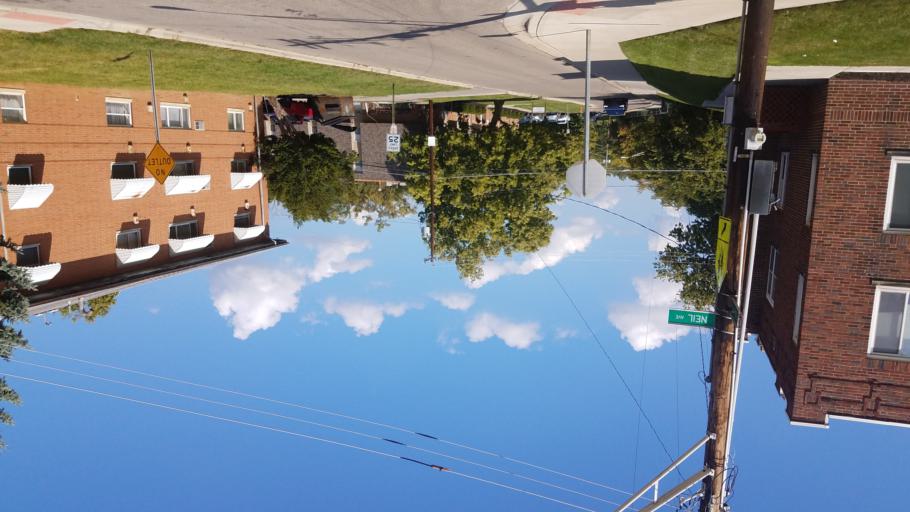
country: US
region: Ohio
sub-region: Franklin County
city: Grandview Heights
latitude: 40.0092
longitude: -83.0137
